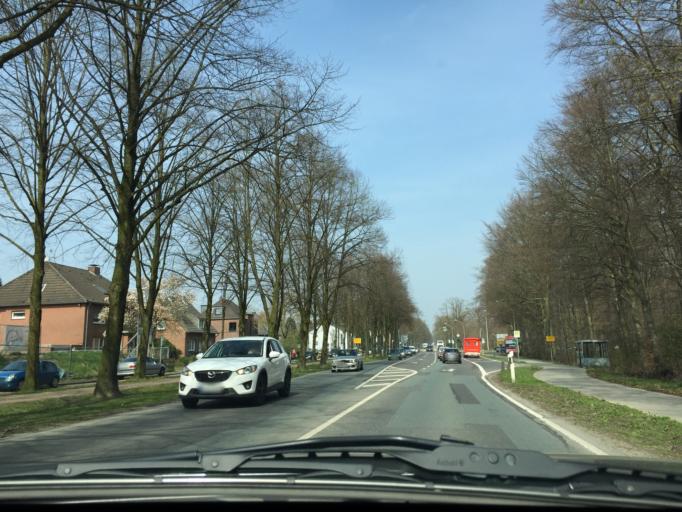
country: DE
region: North Rhine-Westphalia
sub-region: Regierungsbezirk Dusseldorf
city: Kleve
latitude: 51.7723
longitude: 6.1396
